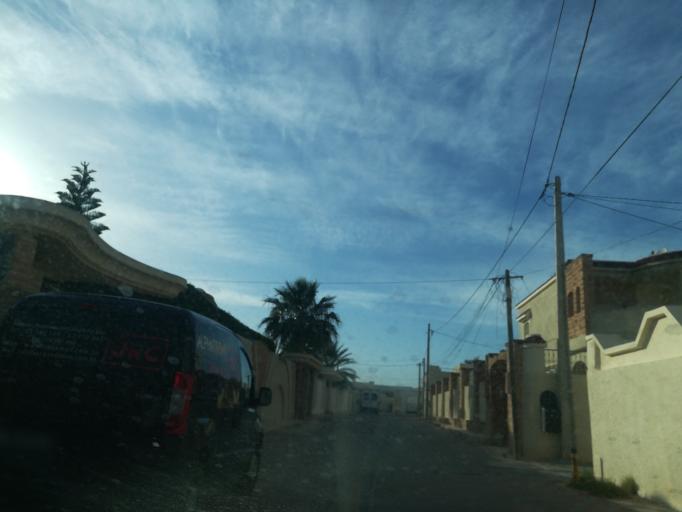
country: TN
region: Safaqis
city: Al Qarmadah
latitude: 34.8085
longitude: 10.7557
